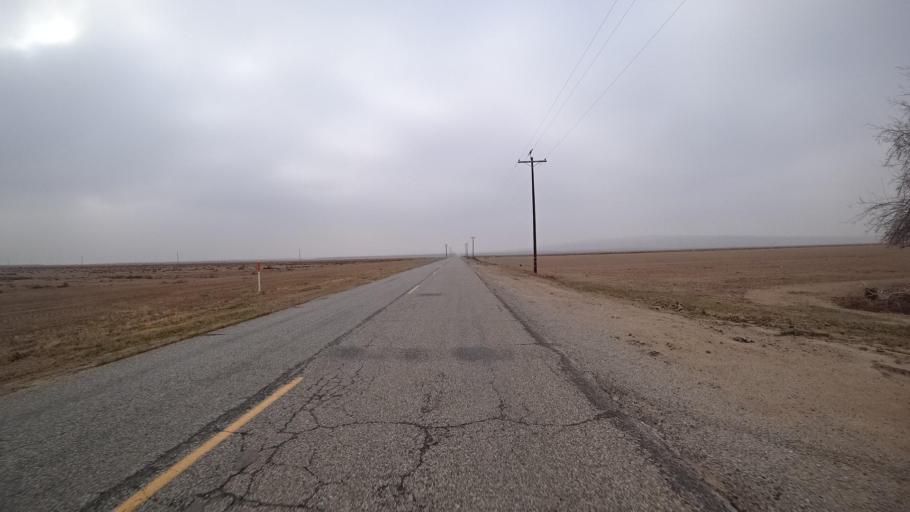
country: US
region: California
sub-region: Kern County
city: Maricopa
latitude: 35.1229
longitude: -119.3195
